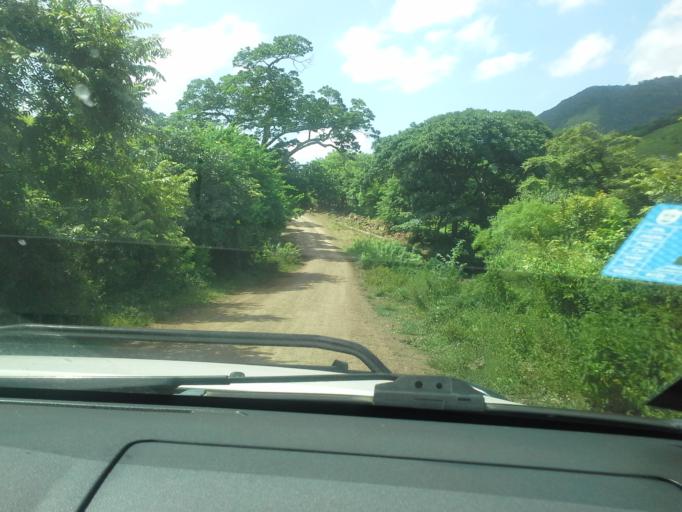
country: NI
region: Matagalpa
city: Terrabona
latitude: 12.7187
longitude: -85.9647
